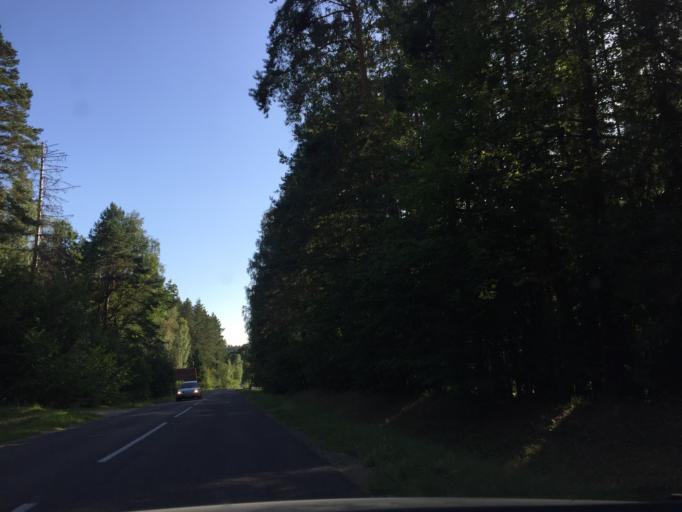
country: LT
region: Panevezys
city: Rokiskis
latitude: 55.8290
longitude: 25.8728
